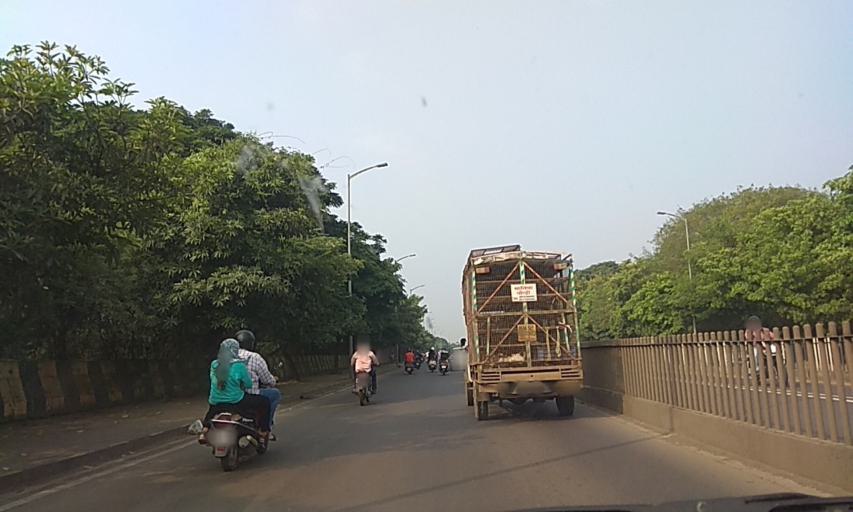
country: IN
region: Maharashtra
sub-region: Pune Division
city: Shivaji Nagar
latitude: 18.5428
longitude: 73.8746
